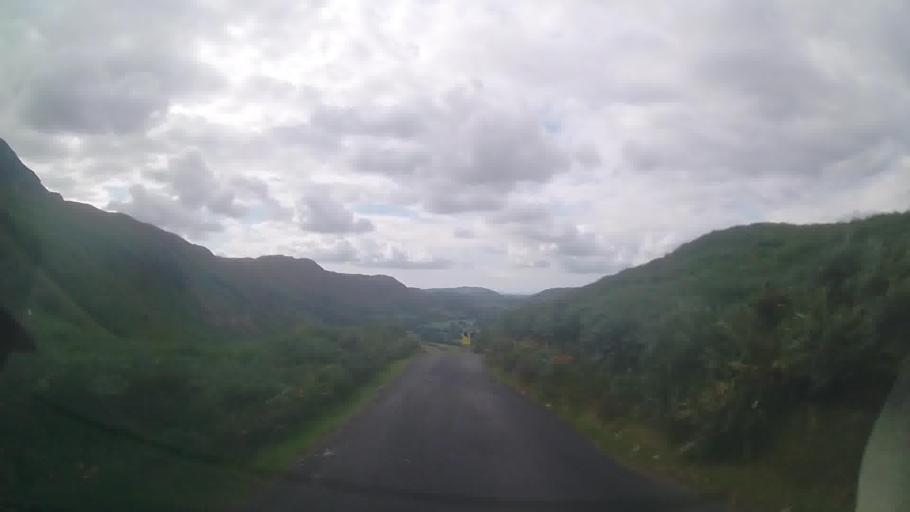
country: GB
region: England
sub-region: Cumbria
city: Millom
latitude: 54.4010
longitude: -3.2067
